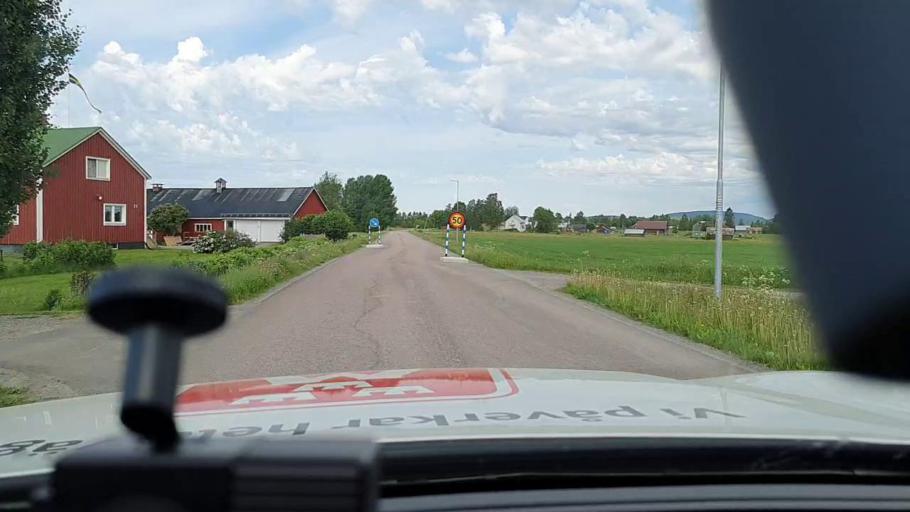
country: SE
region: Norrbotten
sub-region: Bodens Kommun
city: Saevast
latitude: 65.6842
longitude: 21.7944
